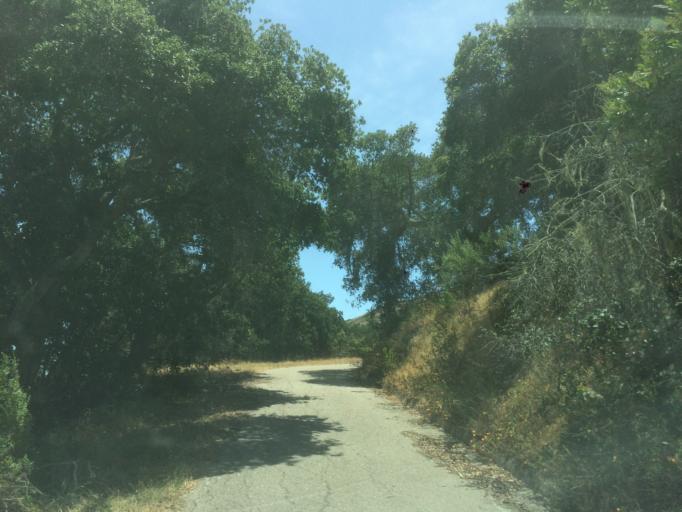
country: US
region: California
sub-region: San Luis Obispo County
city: San Luis Obispo
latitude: 35.2550
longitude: -120.6996
